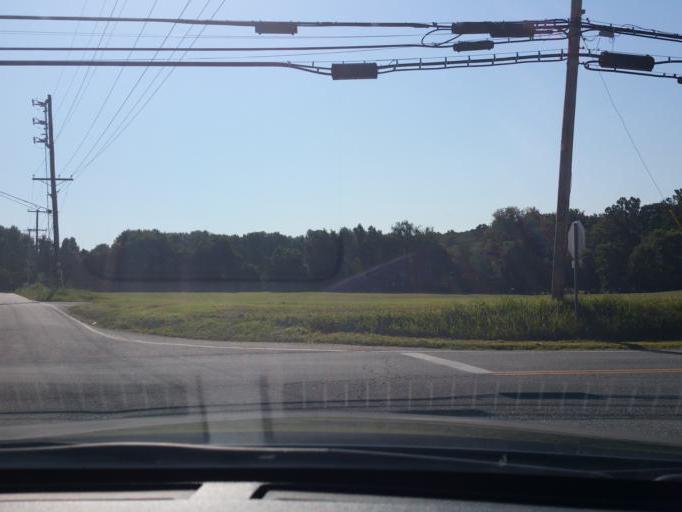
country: US
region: Maryland
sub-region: Cecil County
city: Rising Sun
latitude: 39.6414
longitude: -76.1263
